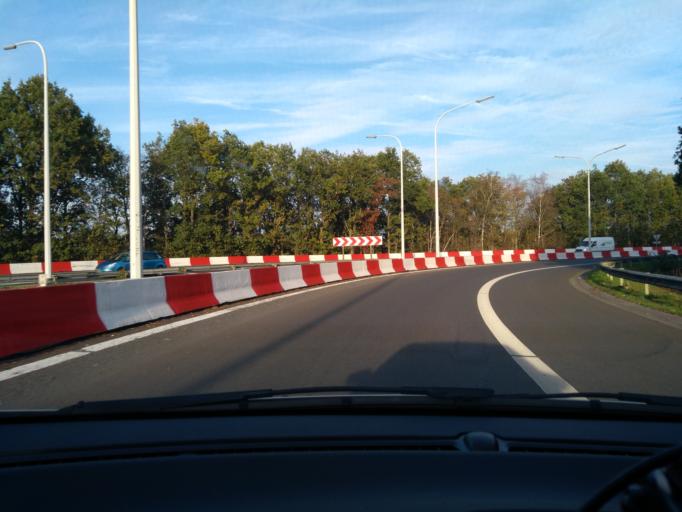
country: BE
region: Wallonia
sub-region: Province du Hainaut
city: Saint-Ghislain
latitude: 50.4544
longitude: 3.8287
